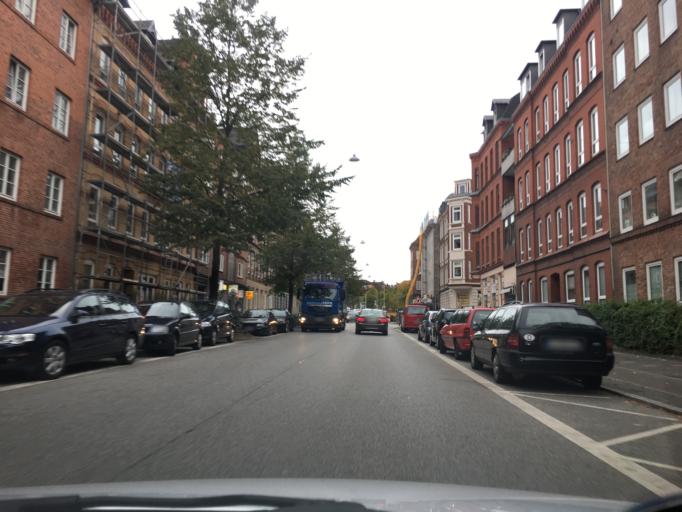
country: DE
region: Schleswig-Holstein
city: Kiel
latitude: 54.3229
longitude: 10.1250
